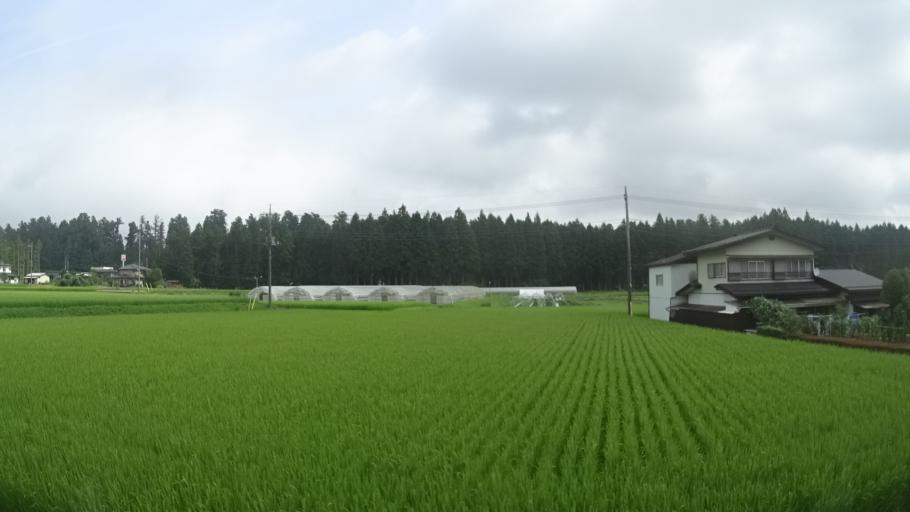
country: JP
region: Tochigi
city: Imaichi
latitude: 36.7285
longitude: 139.6652
